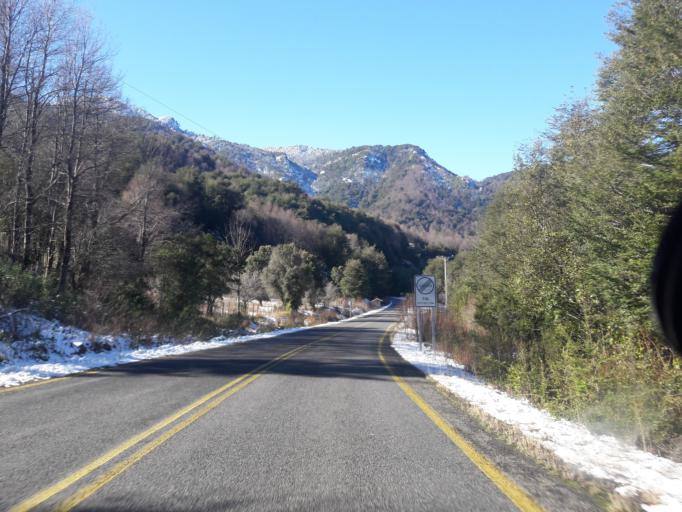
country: CL
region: Araucania
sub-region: Provincia de Cautin
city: Vilcun
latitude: -38.4610
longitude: -71.7135
